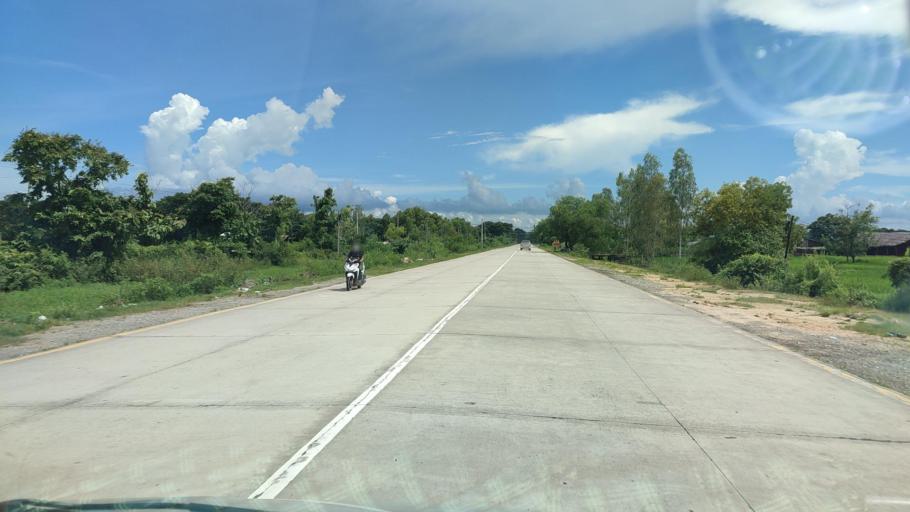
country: MM
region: Bago
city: Nyaunglebin
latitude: 17.9728
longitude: 96.7100
